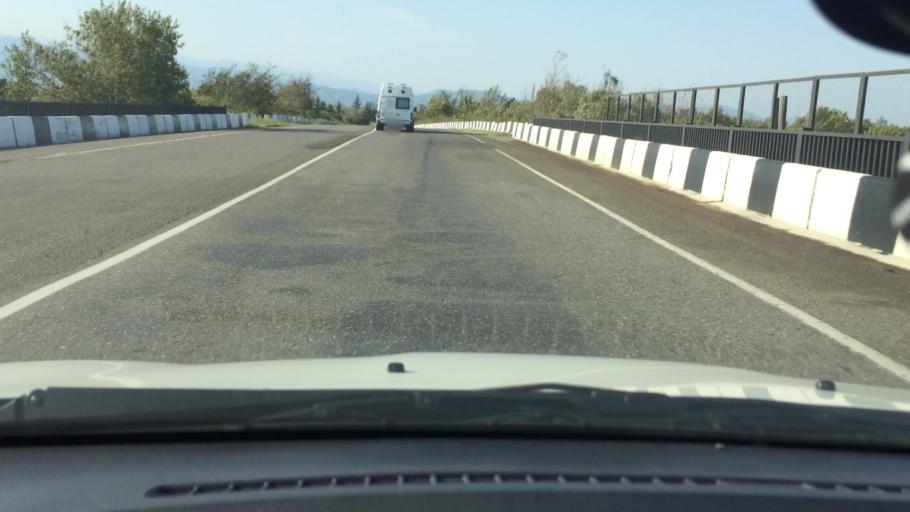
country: GE
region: Imereti
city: Vani
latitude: 42.1894
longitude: 42.4804
